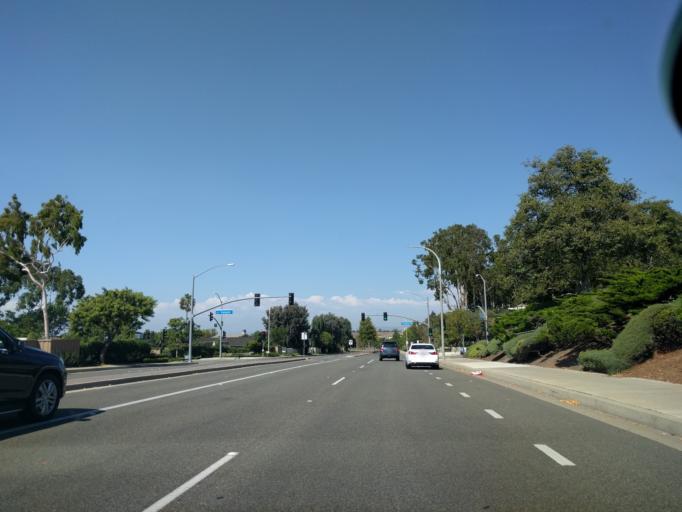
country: US
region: California
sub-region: Orange County
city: San Joaquin Hills
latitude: 33.6203
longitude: -117.8522
